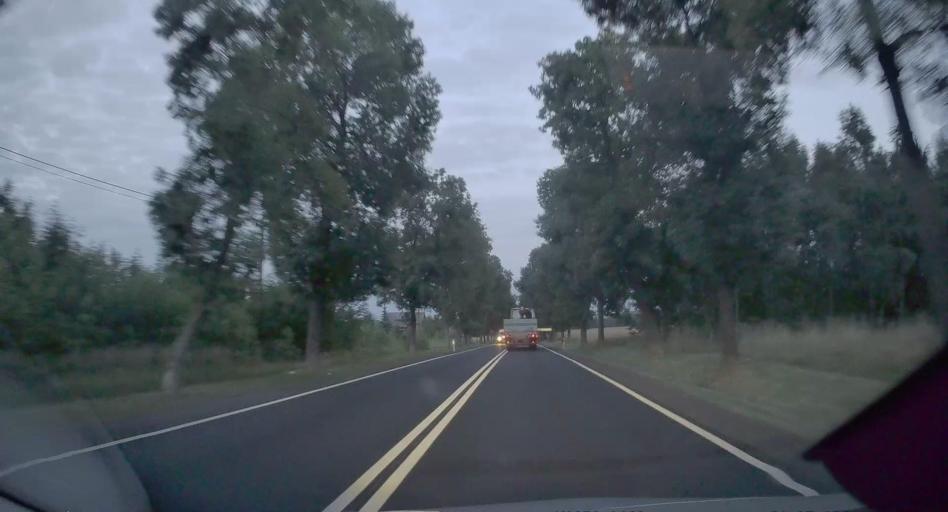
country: PL
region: Silesian Voivodeship
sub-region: Powiat klobucki
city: Opatow
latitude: 50.9548
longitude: 18.7976
